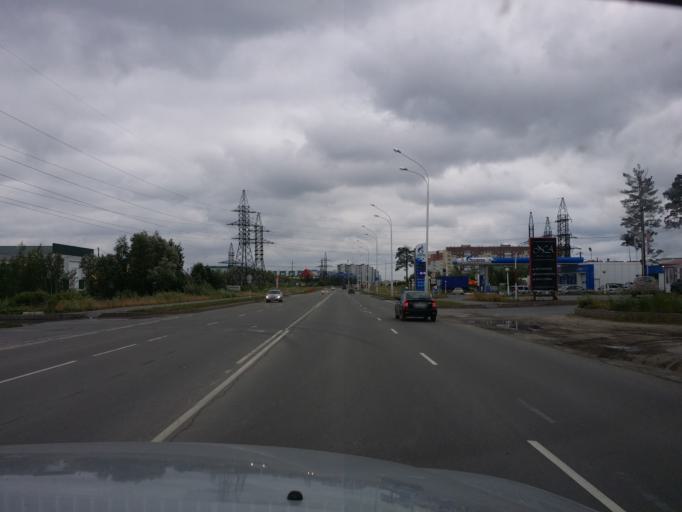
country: RU
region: Khanty-Mansiyskiy Avtonomnyy Okrug
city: Nizhnevartovsk
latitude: 60.9619
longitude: 76.5567
